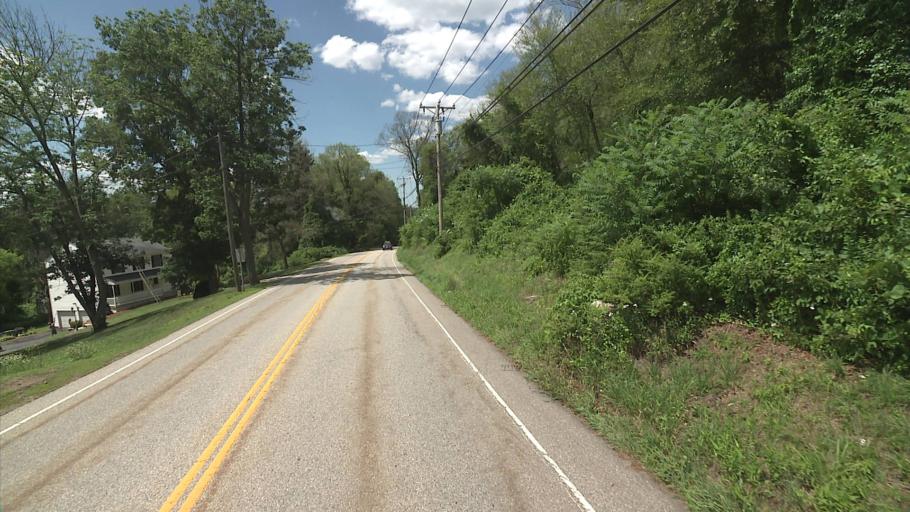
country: US
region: Connecticut
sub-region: Middlesex County
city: Higganum
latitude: 41.5349
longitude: -72.5427
